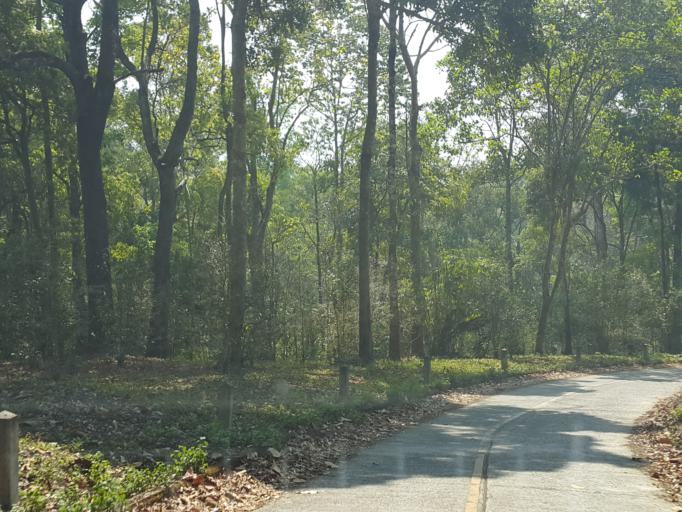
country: TH
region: Chiang Mai
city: Mae On
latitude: 18.8369
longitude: 99.3744
